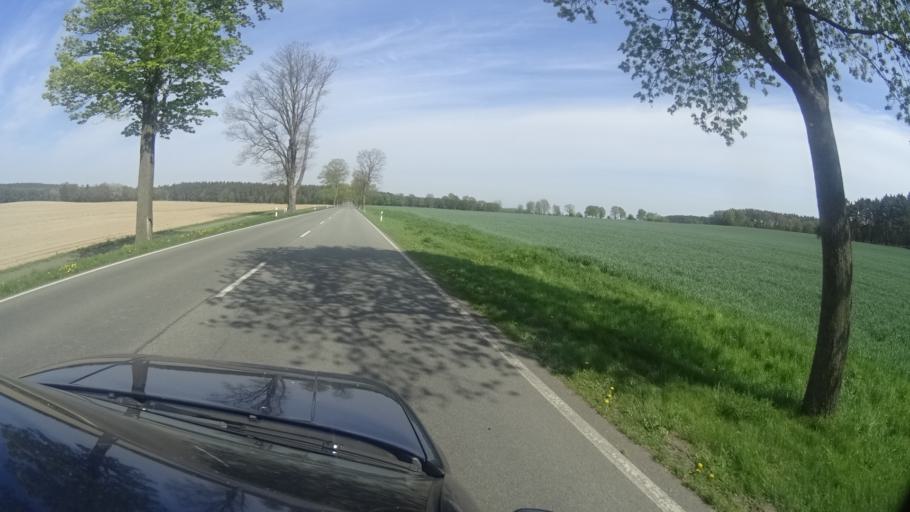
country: DE
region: Brandenburg
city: Friesack
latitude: 52.7110
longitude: 12.5949
